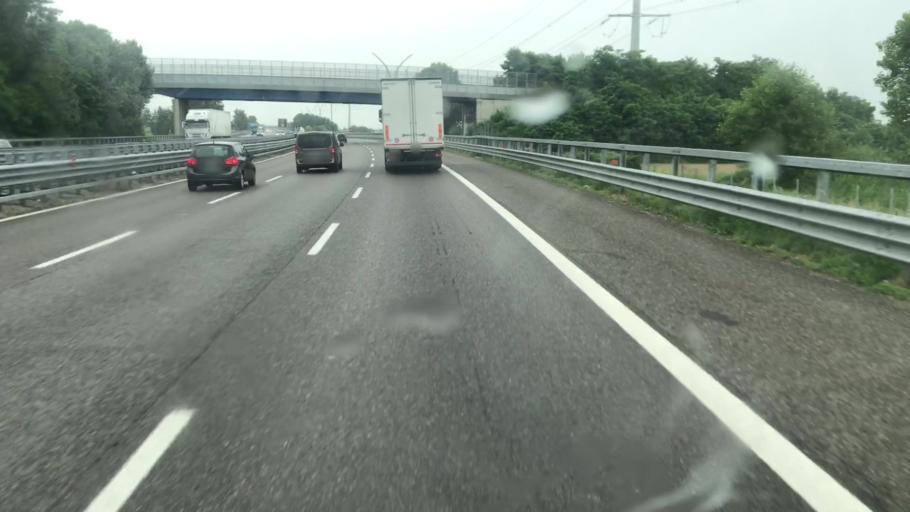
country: IT
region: Lombardy
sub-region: Provincia di Pavia
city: Trivolzio
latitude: 45.2628
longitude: 9.0530
